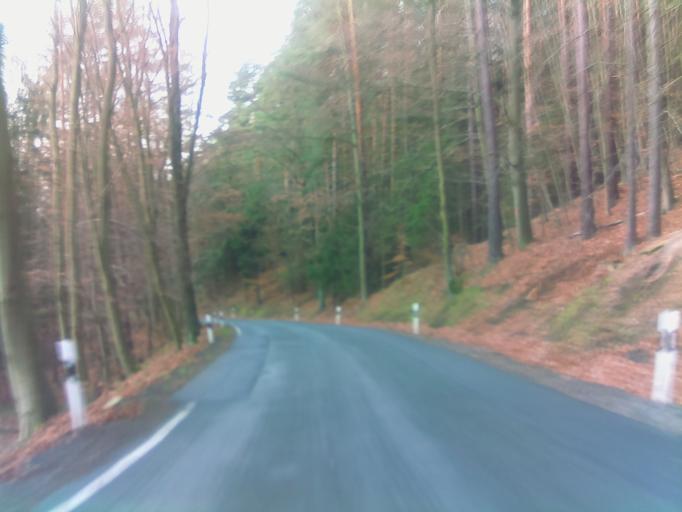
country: DE
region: Thuringia
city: Albersdorf
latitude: 50.8903
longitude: 11.7685
